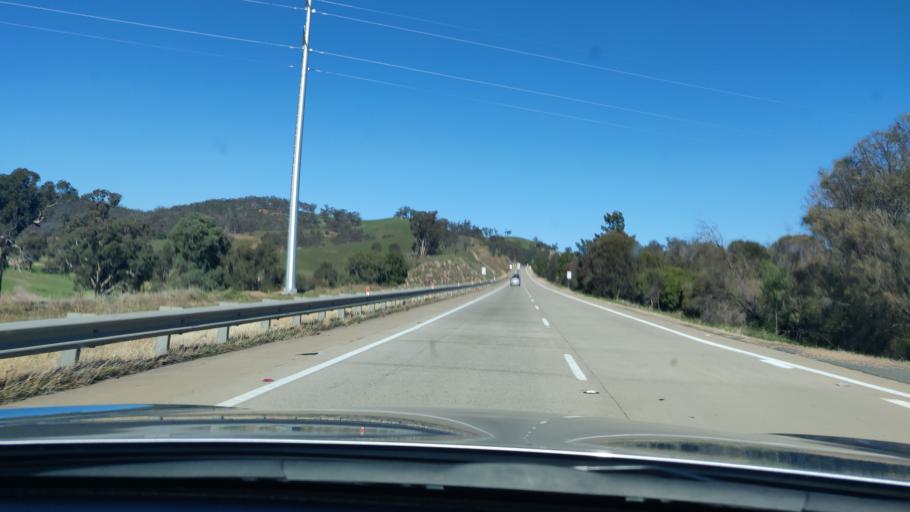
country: AU
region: New South Wales
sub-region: Gundagai
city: Gundagai
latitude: -35.2062
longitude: 147.8148
